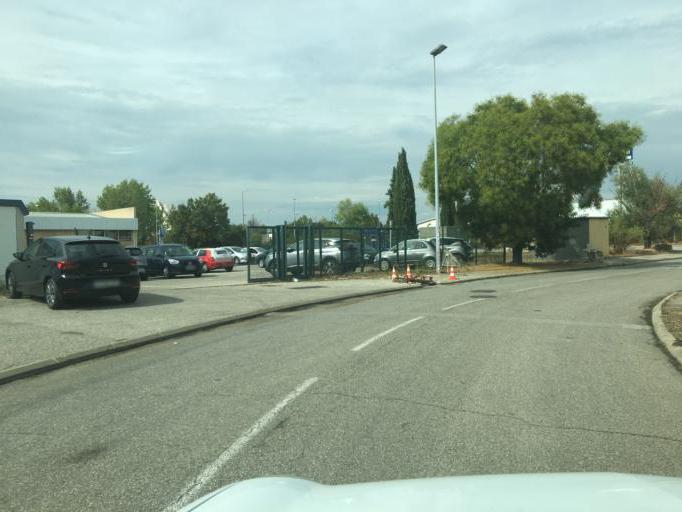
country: FR
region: Provence-Alpes-Cote d'Azur
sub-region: Departement des Bouches-du-Rhone
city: Bouc-Bel-Air
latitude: 43.4847
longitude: 5.3852
